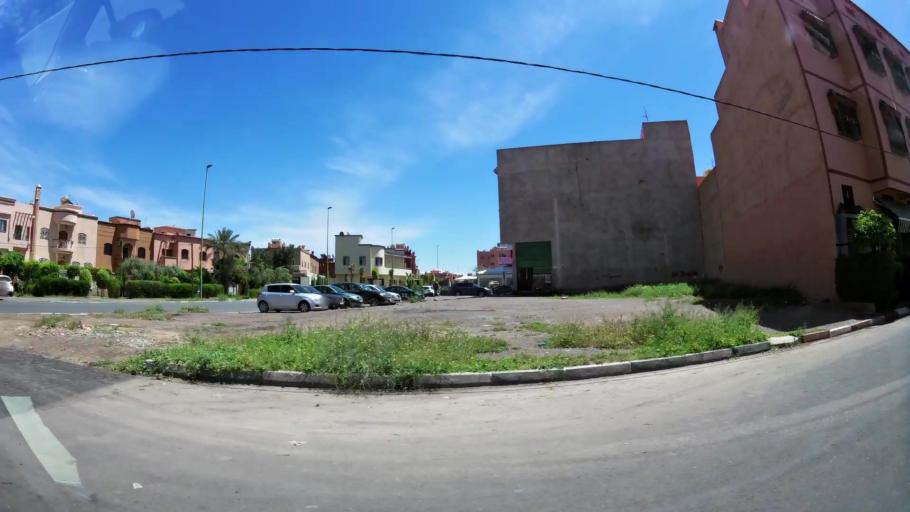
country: MA
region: Marrakech-Tensift-Al Haouz
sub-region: Marrakech
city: Marrakesh
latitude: 31.6422
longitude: -8.0469
